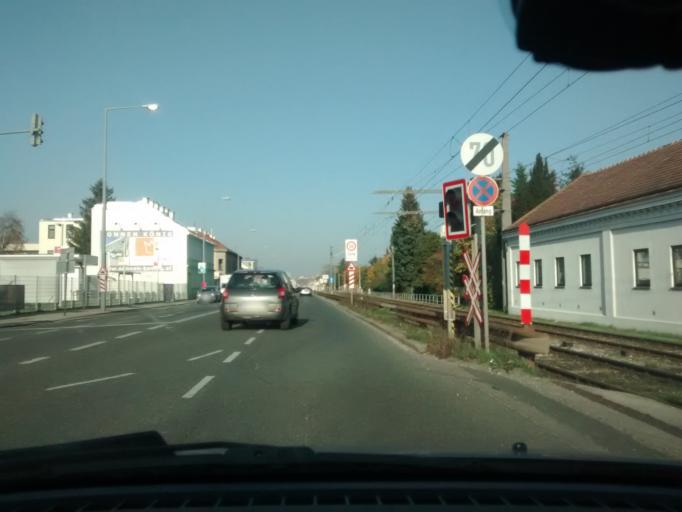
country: AT
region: Lower Austria
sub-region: Politischer Bezirk Modling
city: Vosendorf
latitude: 48.1377
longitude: 16.3264
